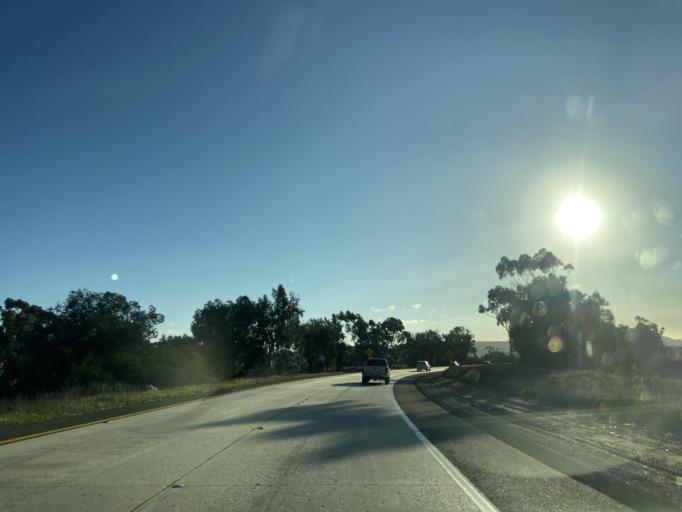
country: US
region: California
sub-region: San Diego County
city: Imperial Beach
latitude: 32.5701
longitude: -117.0415
